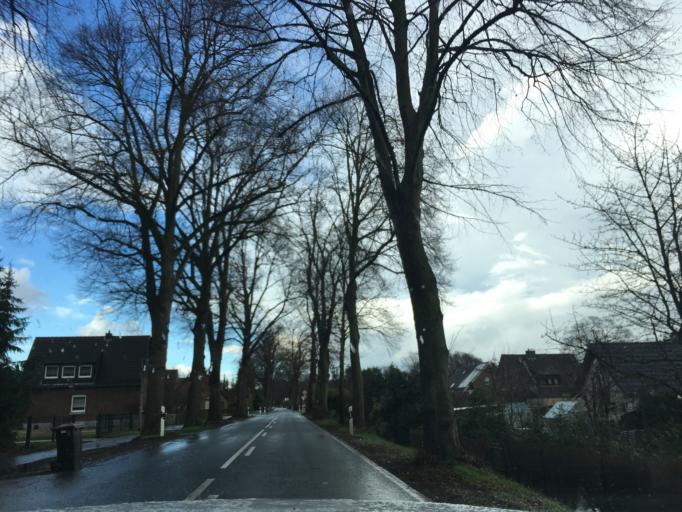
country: DE
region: North Rhine-Westphalia
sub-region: Regierungsbezirk Munster
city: Isselburg
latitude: 51.7798
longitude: 6.4637
